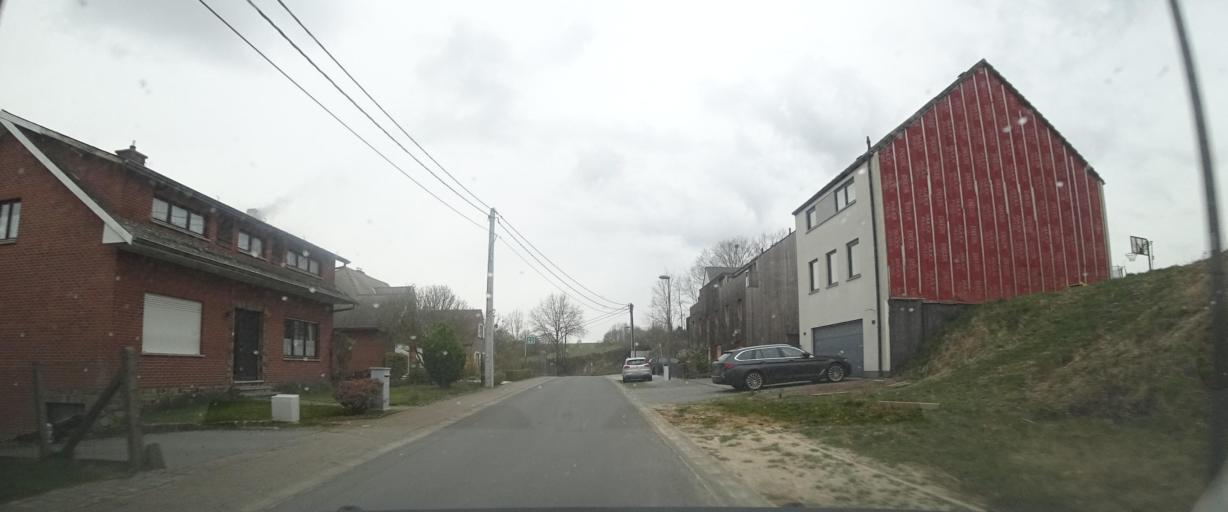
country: BE
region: Wallonia
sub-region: Province du Brabant Wallon
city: Mont-Saint-Guibert
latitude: 50.6315
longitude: 4.6059
